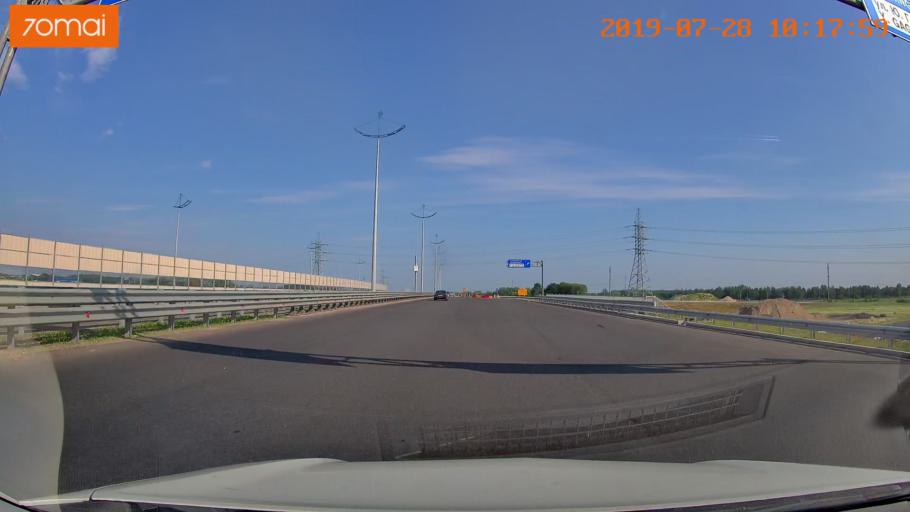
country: RU
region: Kaliningrad
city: Maloye Isakovo
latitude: 54.7457
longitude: 20.5919
